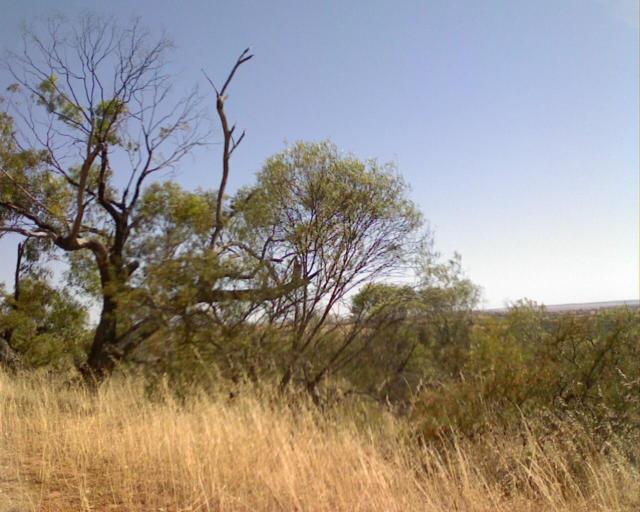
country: AU
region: Western Australia
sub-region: Irwin
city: Dongara
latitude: -29.1865
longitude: 115.4380
